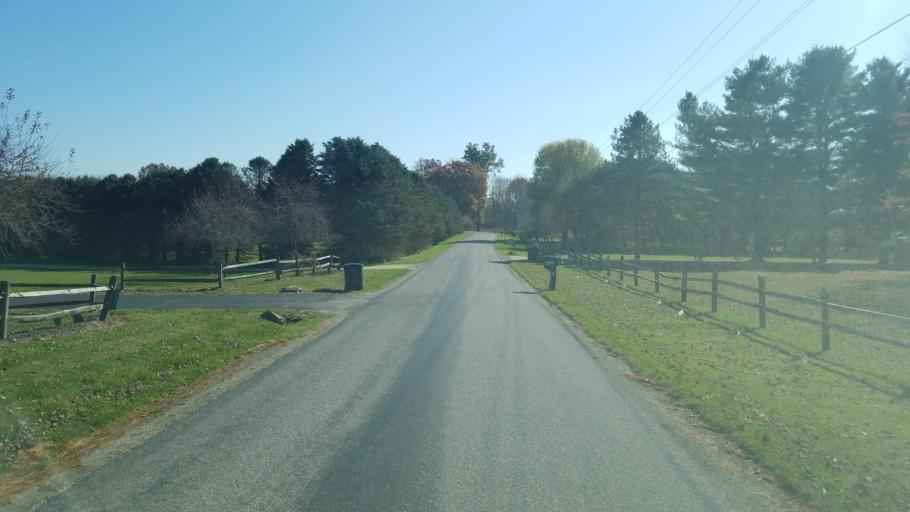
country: US
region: Ohio
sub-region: Licking County
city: Newark
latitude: 40.1238
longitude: -82.3877
